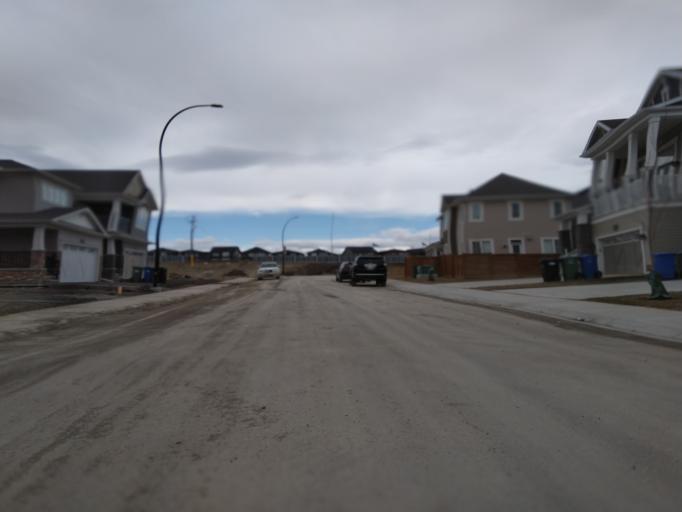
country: CA
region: Alberta
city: Calgary
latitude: 51.1800
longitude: -114.0927
